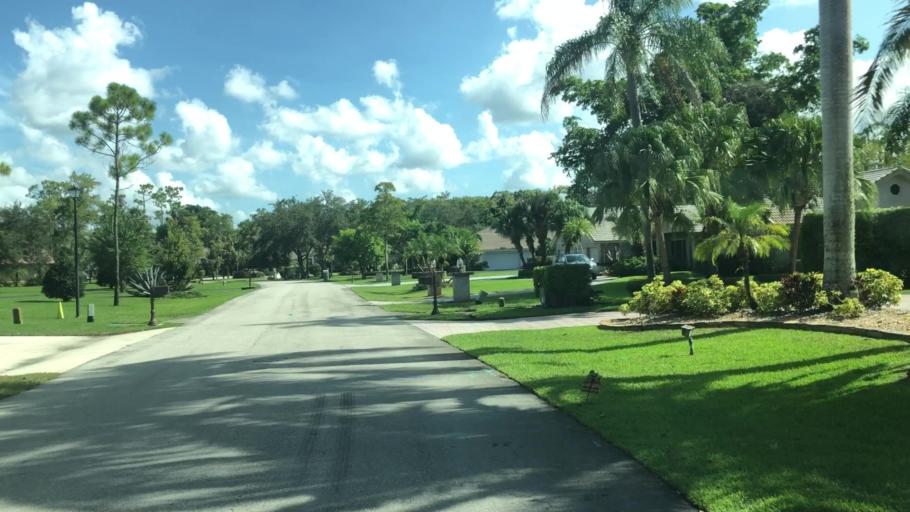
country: US
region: Florida
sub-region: Broward County
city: Parkland
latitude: 26.2917
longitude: -80.2318
